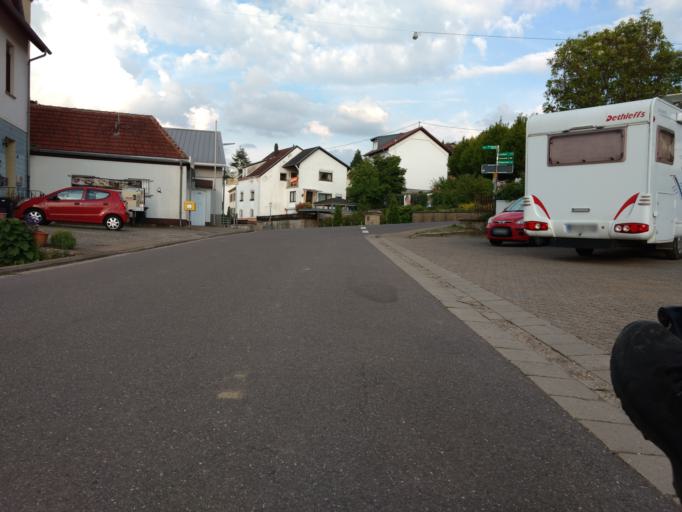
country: DE
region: Saarland
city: Beckingen
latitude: 49.4072
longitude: 6.6684
